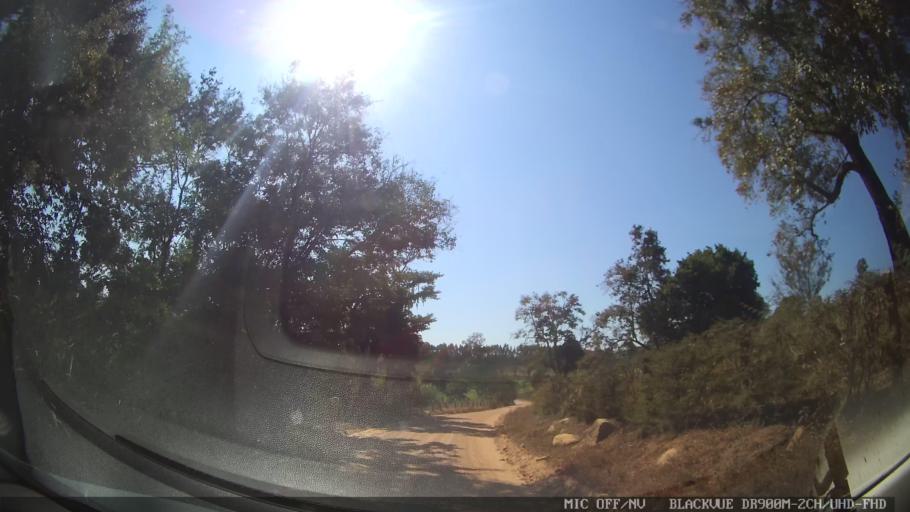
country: BR
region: Sao Paulo
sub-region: Itupeva
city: Itupeva
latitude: -23.0649
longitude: -47.0931
